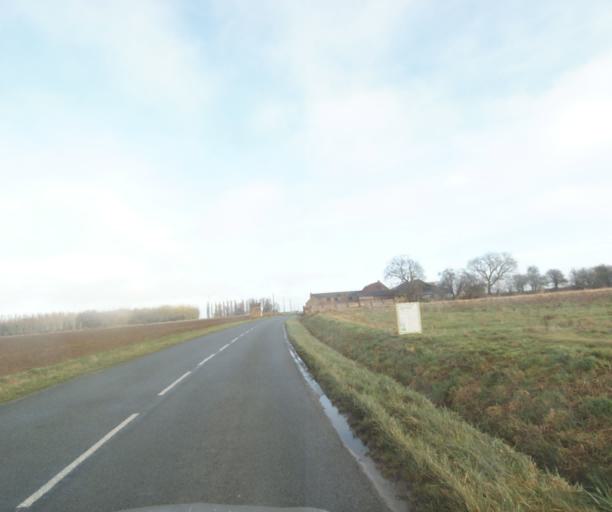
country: FR
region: Nord-Pas-de-Calais
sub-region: Departement du Nord
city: Haspres
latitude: 50.2734
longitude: 3.4327
